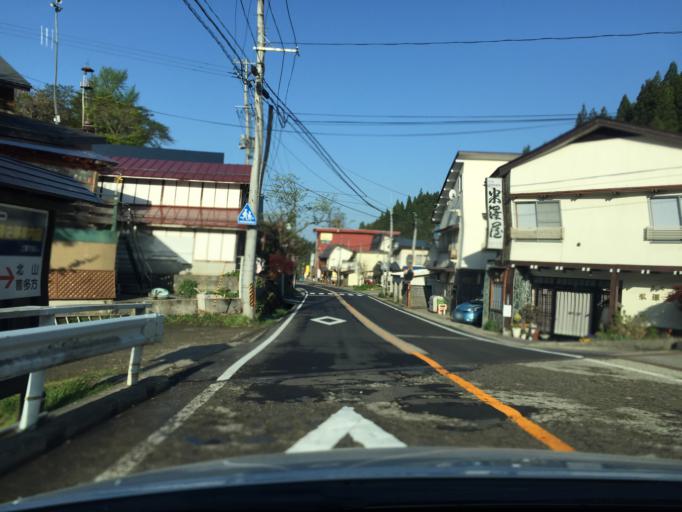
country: JP
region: Fukushima
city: Kitakata
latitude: 37.6691
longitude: 139.9863
